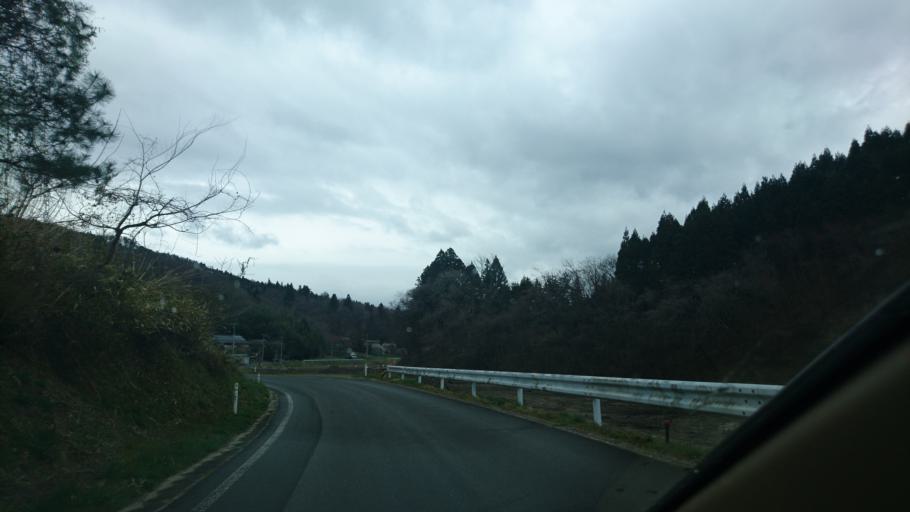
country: JP
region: Iwate
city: Ichinoseki
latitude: 38.9530
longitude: 141.3150
